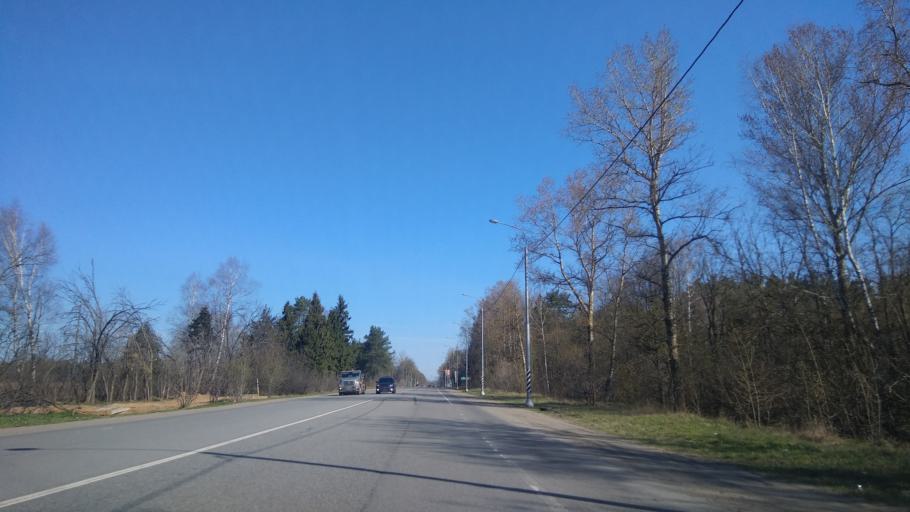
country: RU
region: Moskovskaya
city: Pushkino
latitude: 56.0273
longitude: 37.8711
